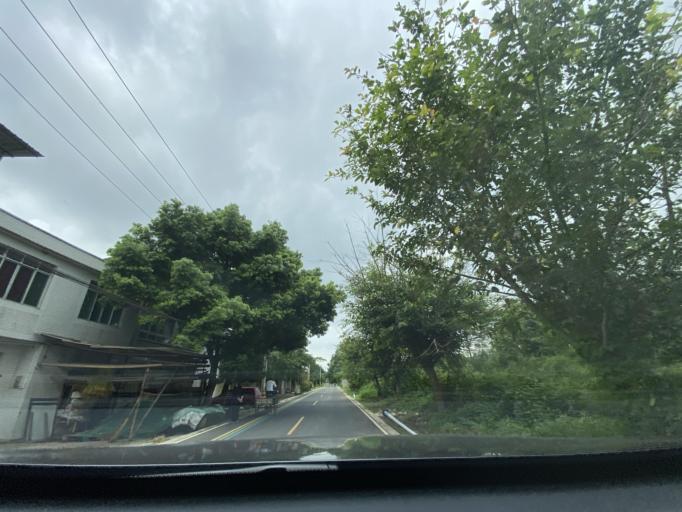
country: CN
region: Sichuan
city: Dongsheng
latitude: 30.4078
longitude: 104.0007
